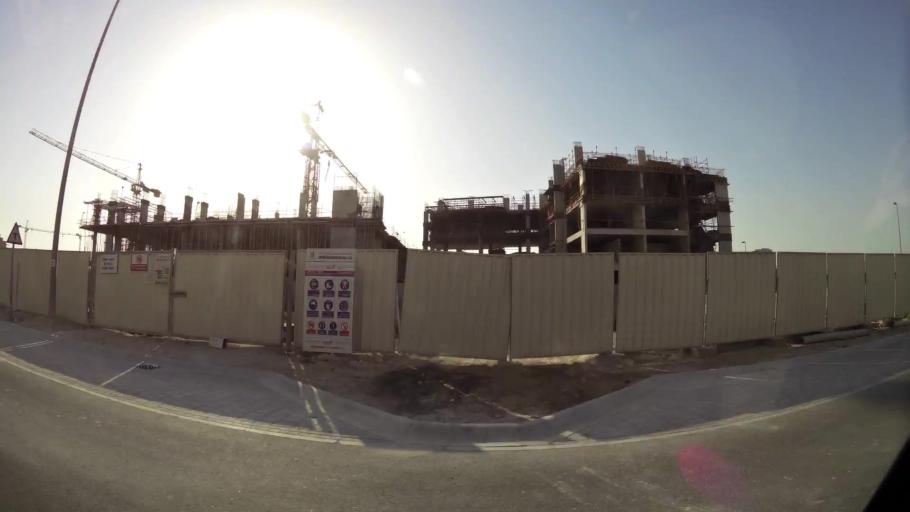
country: AE
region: Dubai
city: Dubai
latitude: 25.0616
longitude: 55.2045
